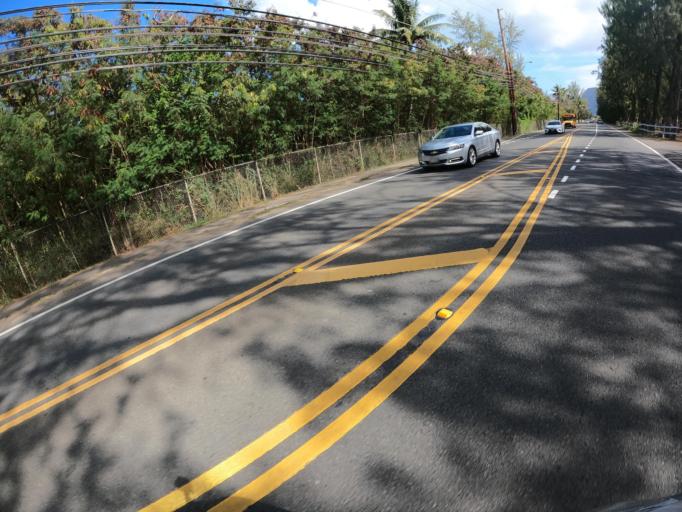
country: US
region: Hawaii
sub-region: Honolulu County
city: Waimanalo Beach
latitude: 21.3435
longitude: -157.7081
